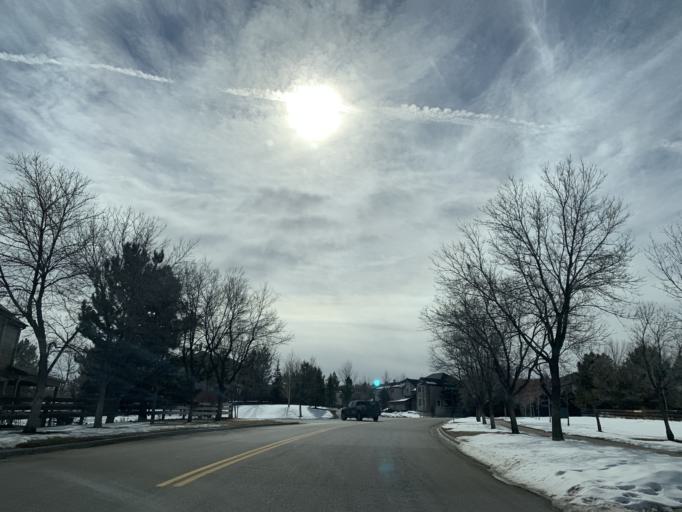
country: US
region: Colorado
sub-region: Douglas County
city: Carriage Club
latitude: 39.5199
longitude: -104.9159
